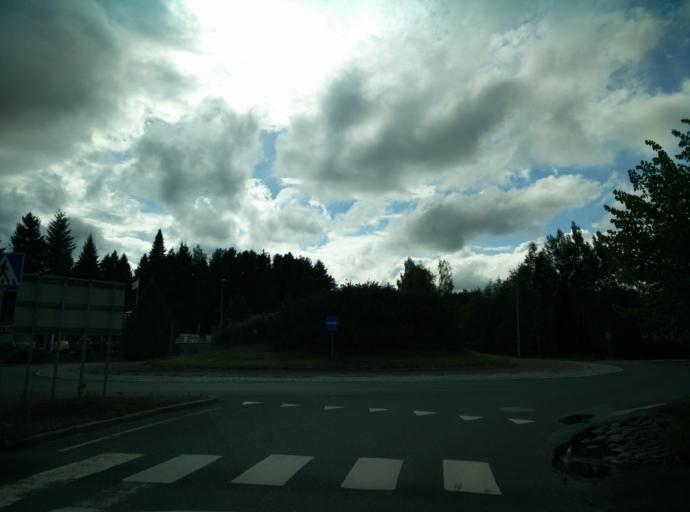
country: FI
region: Haeme
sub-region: Haemeenlinna
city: Kalvola
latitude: 61.0963
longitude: 24.1596
